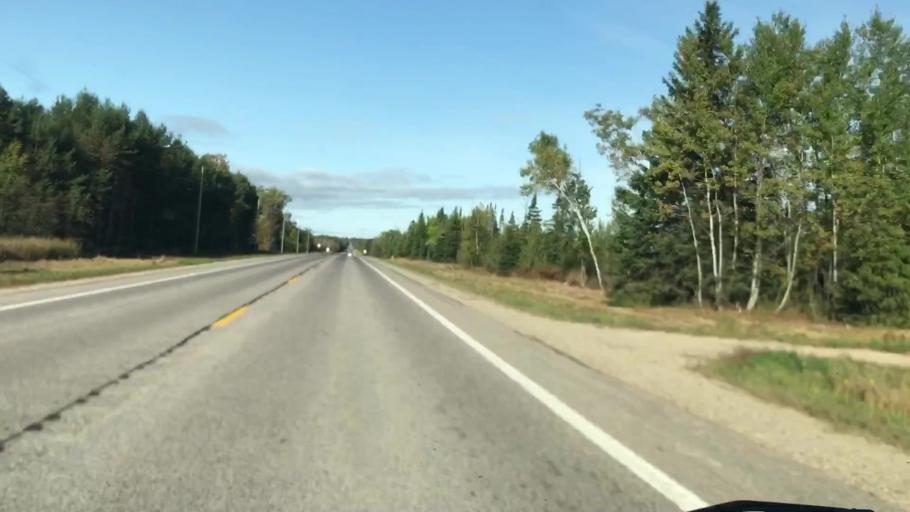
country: US
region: Michigan
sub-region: Luce County
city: Newberry
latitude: 46.3040
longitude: -85.3746
